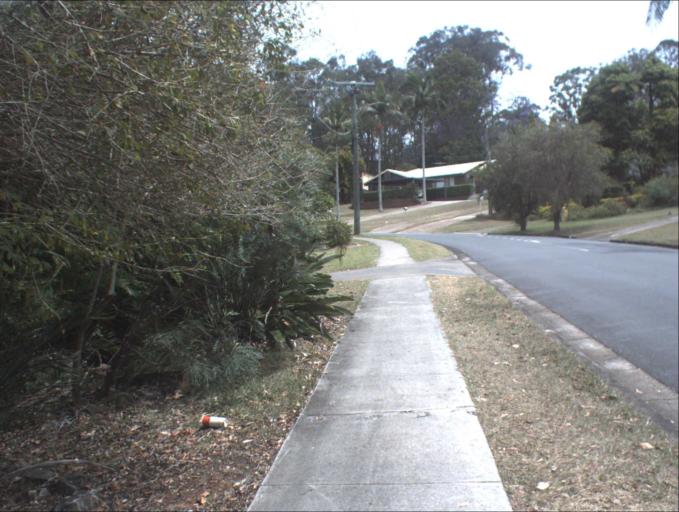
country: AU
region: Queensland
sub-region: Logan
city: Slacks Creek
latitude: -27.6716
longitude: 153.1748
